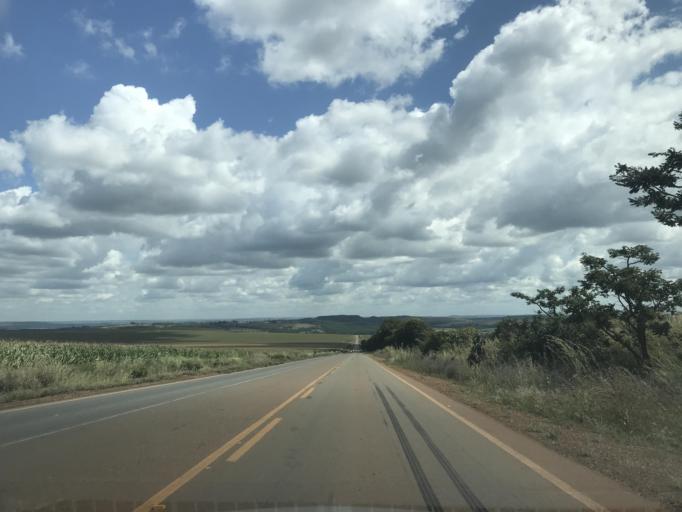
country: BR
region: Goias
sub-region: Vianopolis
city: Vianopolis
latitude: -16.5774
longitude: -48.2981
